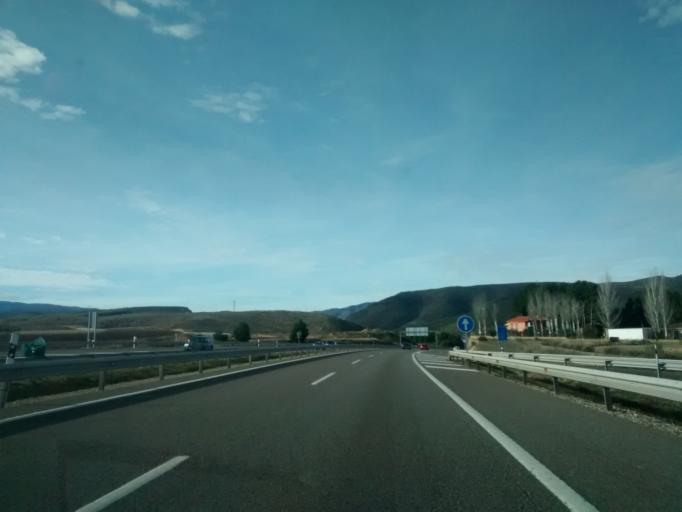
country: ES
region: Aragon
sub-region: Provincia de Zaragoza
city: Ricla
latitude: 41.4793
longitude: -1.4019
